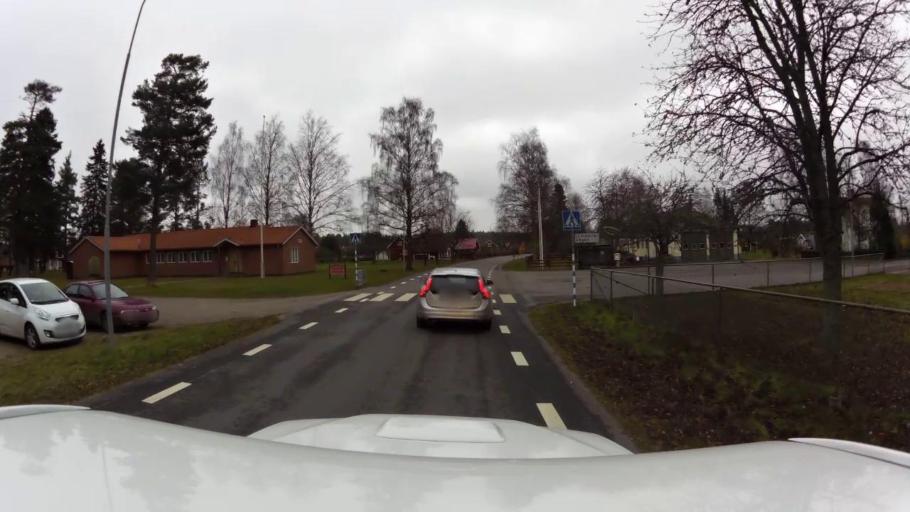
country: SE
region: OEstergoetland
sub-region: Kinda Kommun
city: Kisa
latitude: 58.1233
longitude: 15.4293
